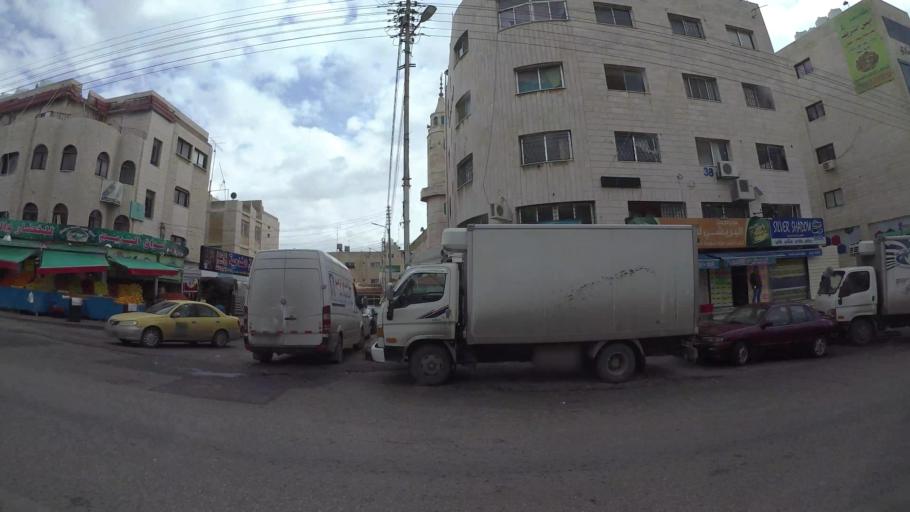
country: JO
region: Amman
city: Amman
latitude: 31.9824
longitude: 35.9242
